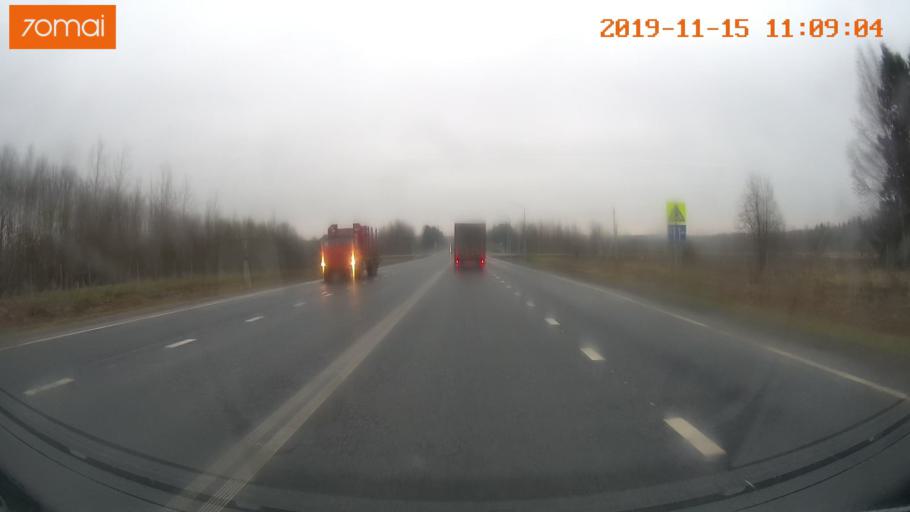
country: RU
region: Vologda
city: Chebsara
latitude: 59.1203
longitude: 39.0894
